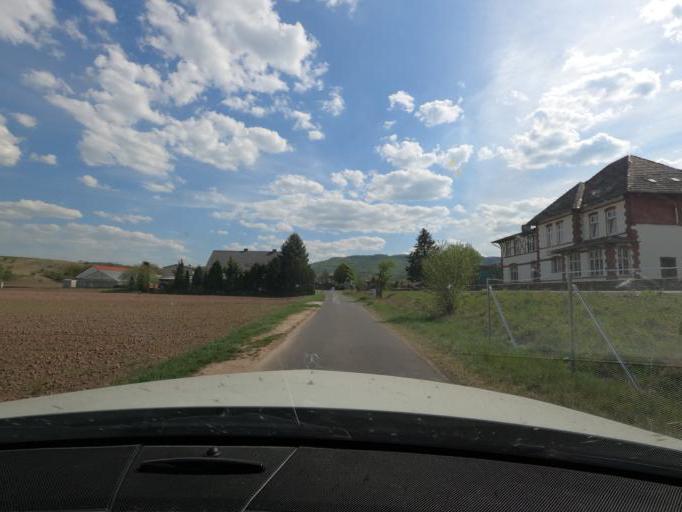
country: DE
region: Hesse
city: Wanfried
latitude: 51.1374
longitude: 10.1864
